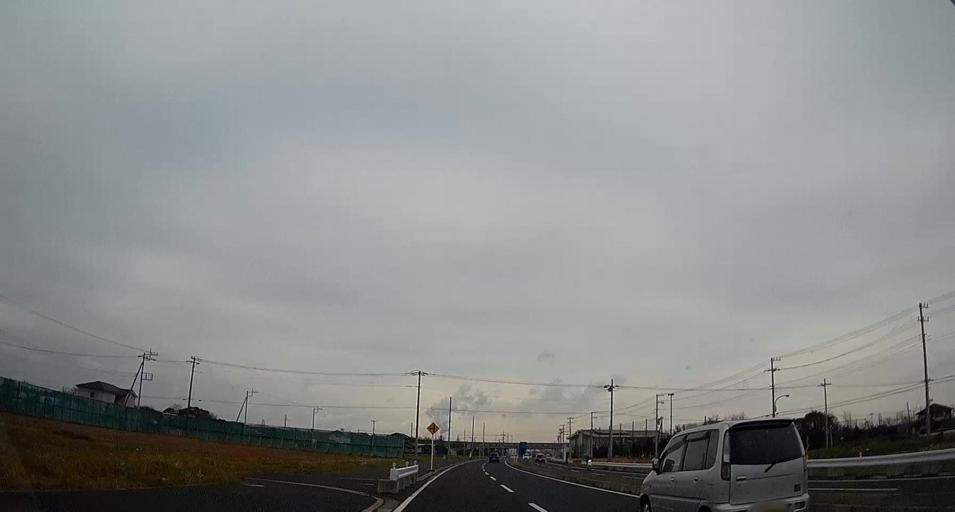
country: JP
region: Chiba
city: Kisarazu
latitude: 35.4268
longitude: 139.9236
